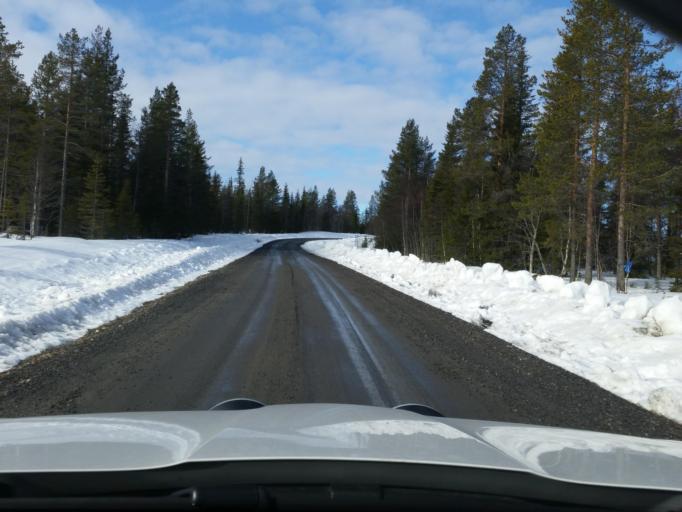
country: SE
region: Vaesterbotten
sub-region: Skelleftea Kommun
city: Storvik
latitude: 65.5067
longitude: 20.3902
